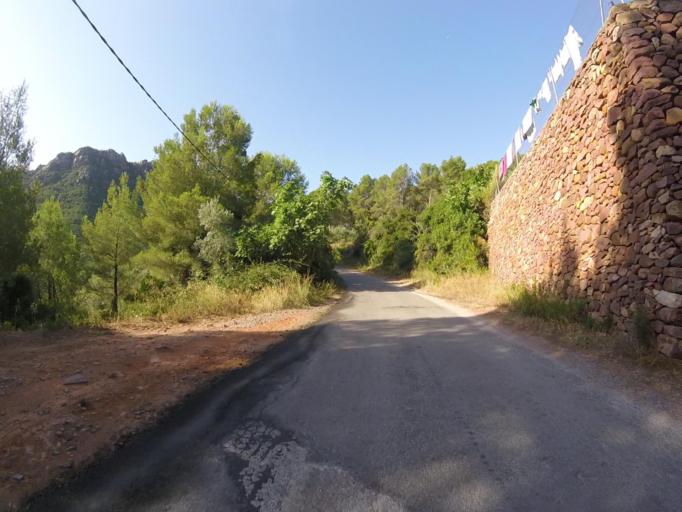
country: ES
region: Valencia
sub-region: Provincia de Castello
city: Benicassim
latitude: 40.0859
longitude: 0.0544
